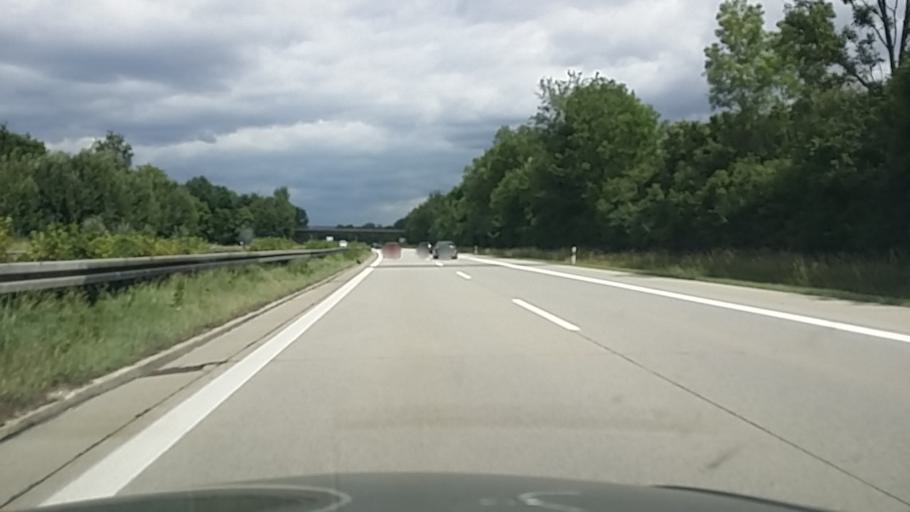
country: DE
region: Bavaria
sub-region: Lower Bavaria
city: Eching
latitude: 48.5132
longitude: 12.0526
